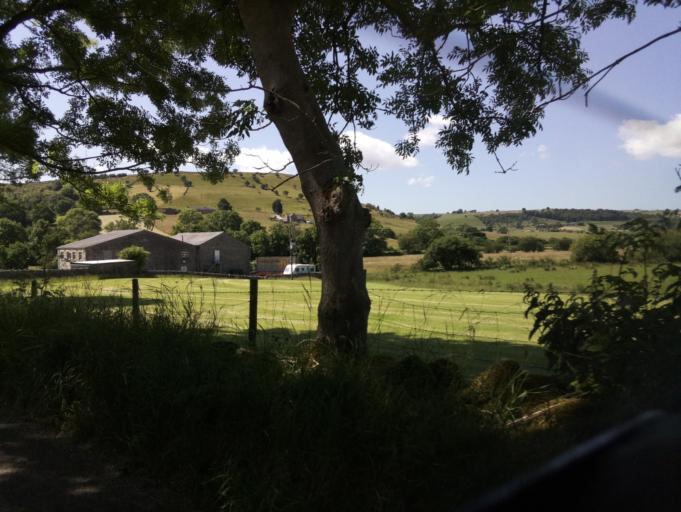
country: GB
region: England
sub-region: Derbyshire
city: Buxton
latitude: 53.1969
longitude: -1.8750
